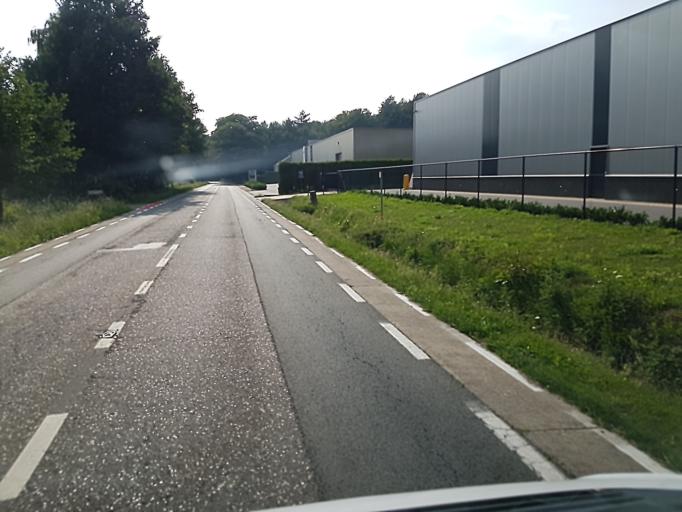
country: BE
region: Flanders
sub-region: Provincie Antwerpen
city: Baarle-Hertog
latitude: 51.3863
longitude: 4.8898
